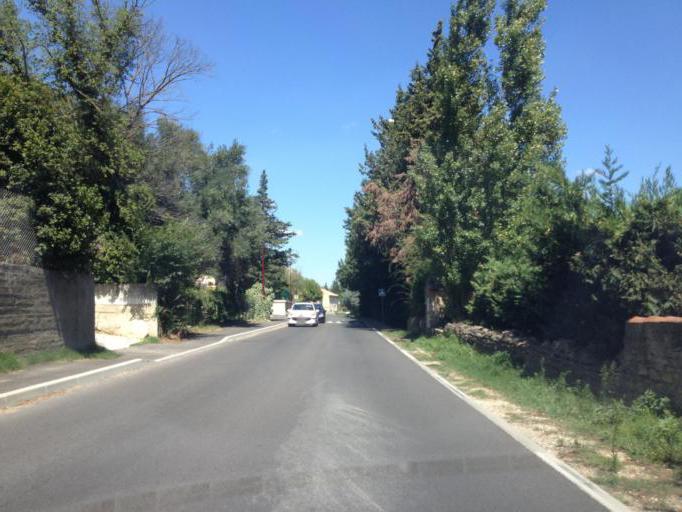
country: FR
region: Languedoc-Roussillon
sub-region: Departement du Gard
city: Sauveterre
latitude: 44.0294
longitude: 4.7958
